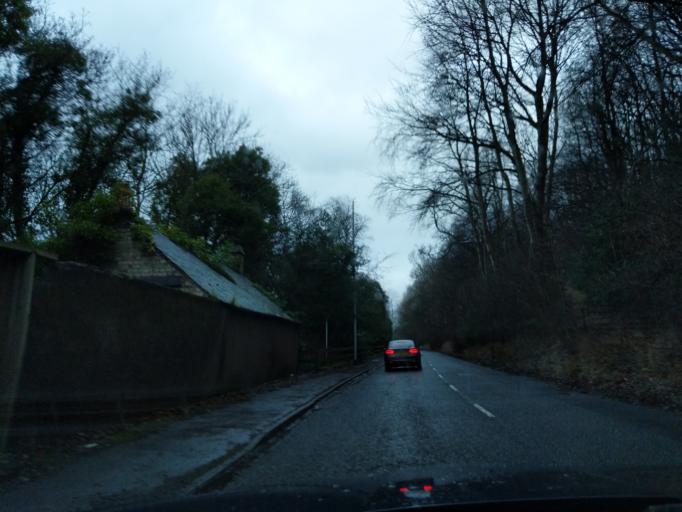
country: GB
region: Scotland
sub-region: The Scottish Borders
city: Galashiels
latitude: 55.6262
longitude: -2.8246
